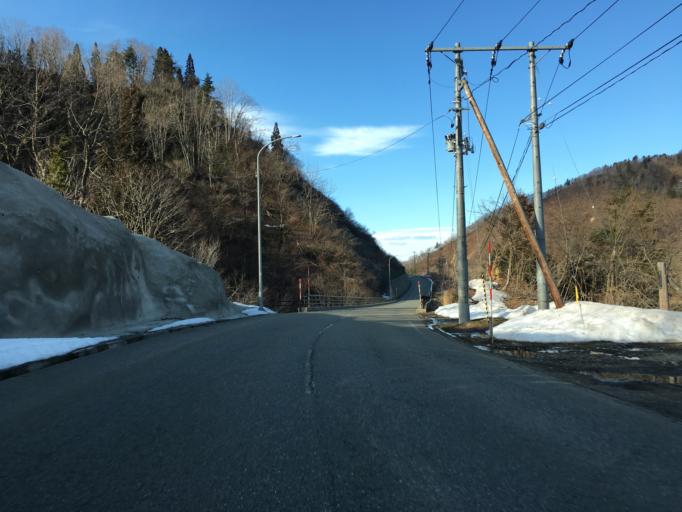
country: JP
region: Yamagata
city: Nagai
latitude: 37.9562
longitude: 139.9165
